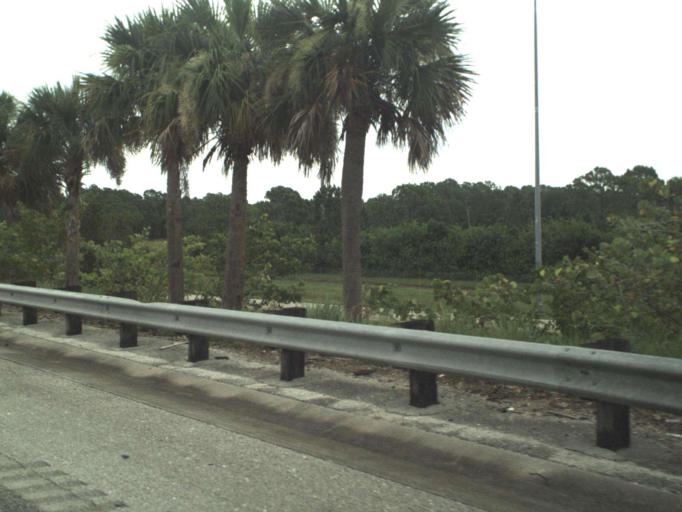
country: US
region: Florida
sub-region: Martin County
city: Hobe Sound
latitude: 27.0459
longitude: -80.2343
